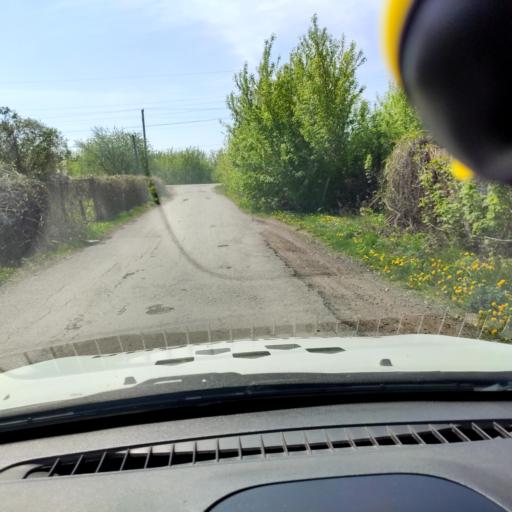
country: RU
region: Samara
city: Tol'yatti
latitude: 53.6635
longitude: 49.3621
